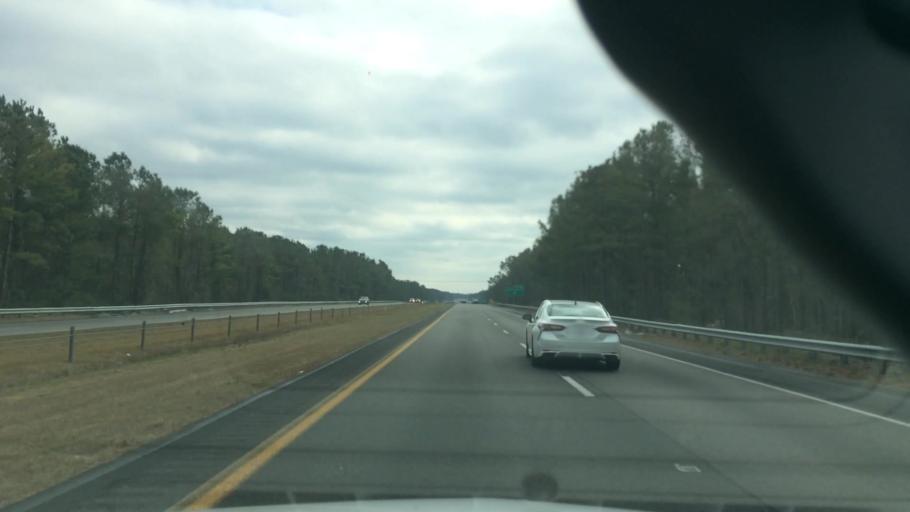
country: US
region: North Carolina
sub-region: New Hanover County
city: Castle Hayne
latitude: 34.3562
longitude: -77.8865
